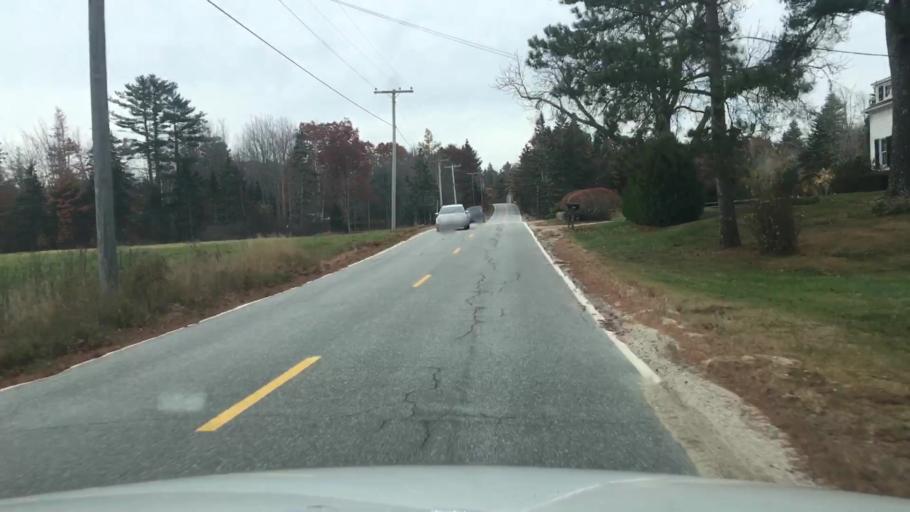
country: US
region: Maine
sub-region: Hancock County
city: Sedgwick
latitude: 44.3289
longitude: -68.5692
